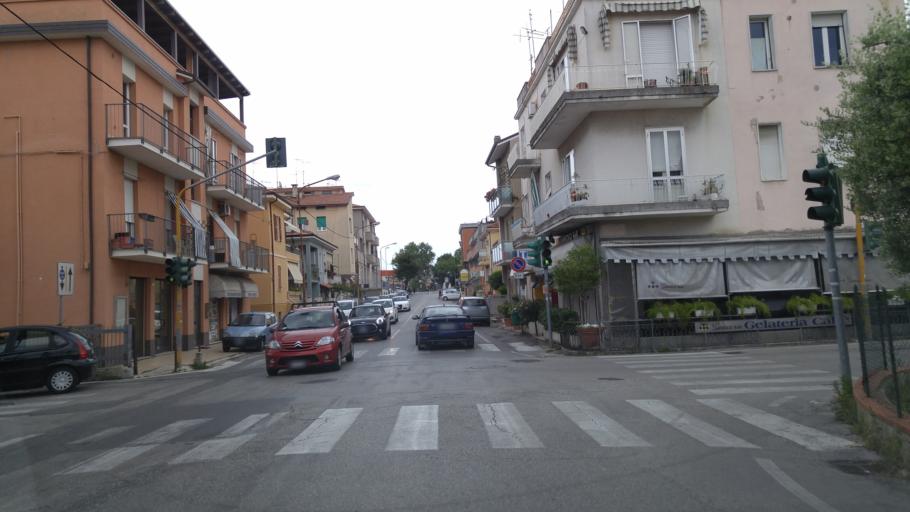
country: IT
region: The Marches
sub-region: Provincia di Pesaro e Urbino
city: Pesaro
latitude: 43.9170
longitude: 12.9008
